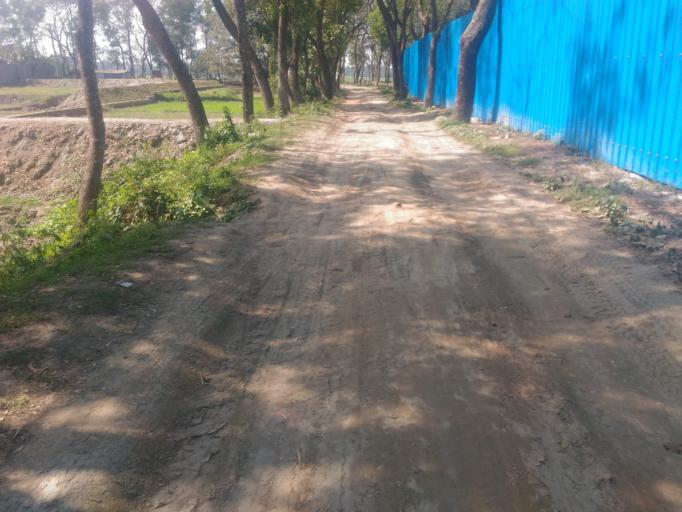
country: BD
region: Dhaka
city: Azimpur
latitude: 23.7852
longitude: 90.2297
